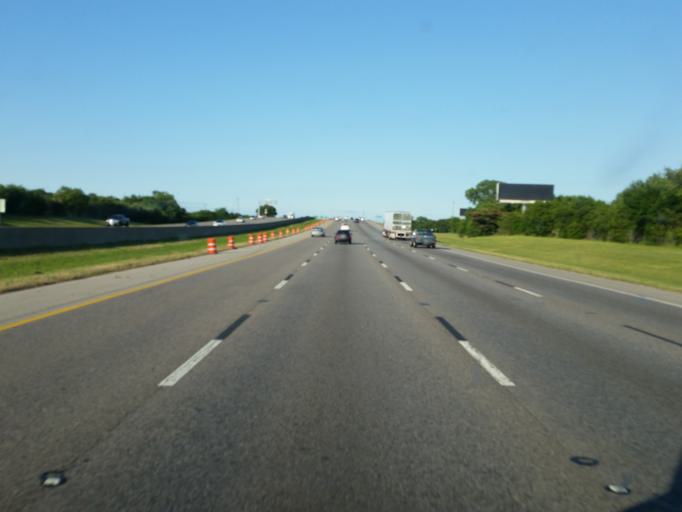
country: US
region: Texas
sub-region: Dallas County
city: Balch Springs
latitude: 32.6854
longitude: -96.6449
